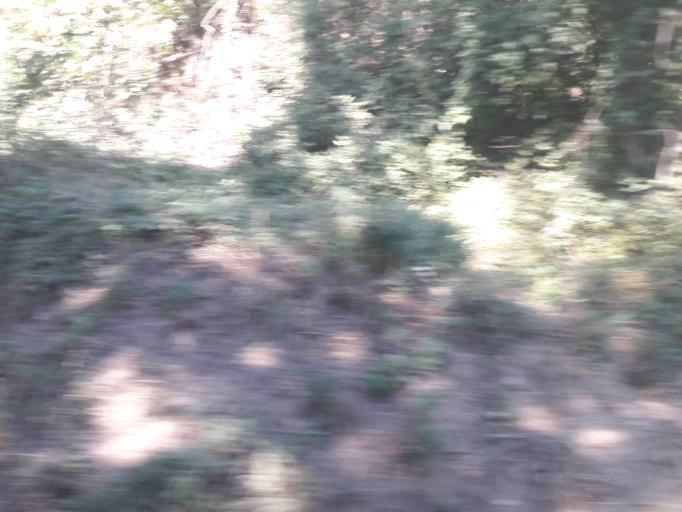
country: DE
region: Baden-Wuerttemberg
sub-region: Karlsruhe Region
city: Ubstadt-Weiher
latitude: 49.1358
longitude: 8.6590
